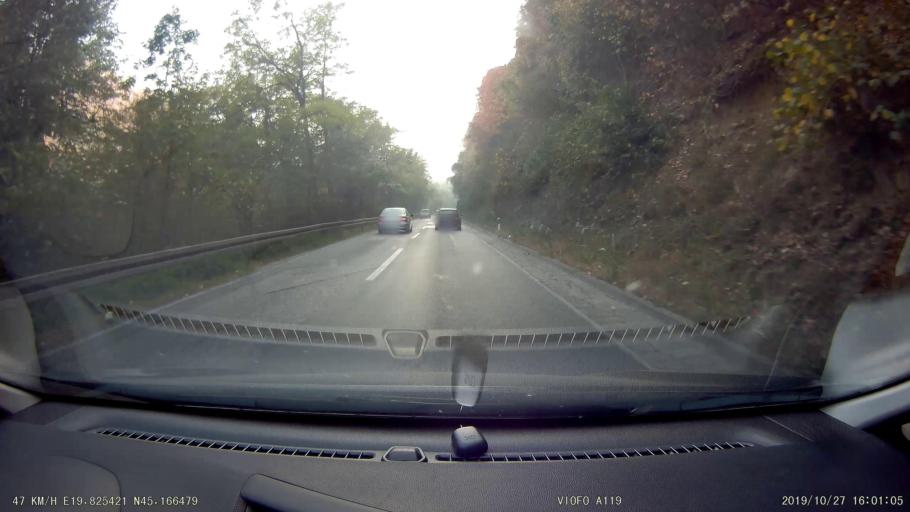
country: RS
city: Vrdnik
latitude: 45.1663
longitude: 19.8255
